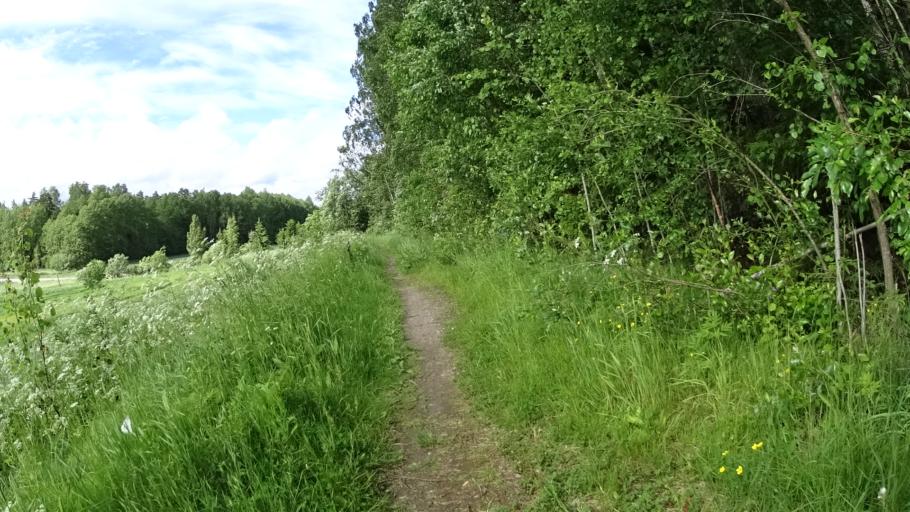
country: FI
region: Uusimaa
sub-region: Helsinki
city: Kilo
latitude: 60.2882
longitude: 24.8059
